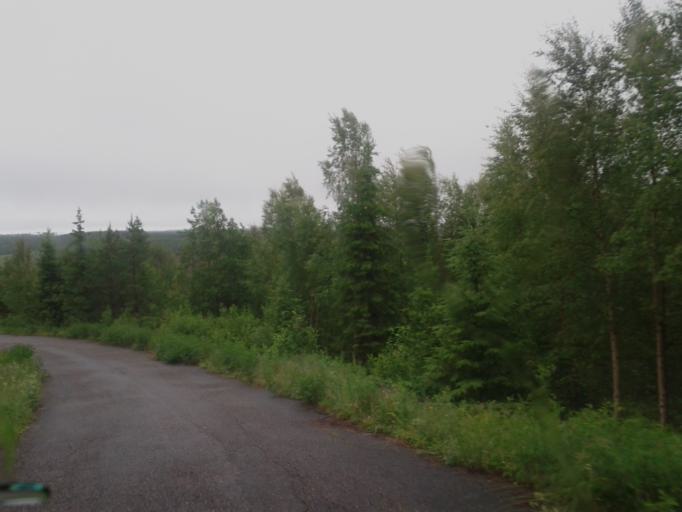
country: SE
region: Vaesternorrland
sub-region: Ange Kommun
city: Fransta
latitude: 62.3859
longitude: 16.3184
